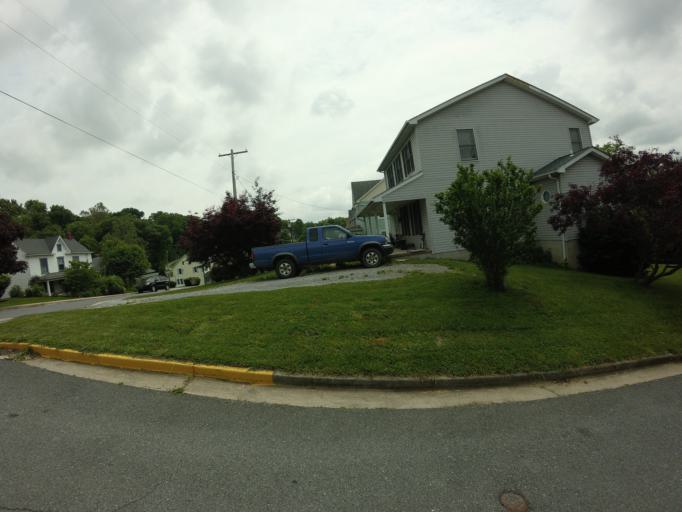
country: US
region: Maryland
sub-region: Frederick County
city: Brunswick
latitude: 39.3128
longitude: -77.6242
